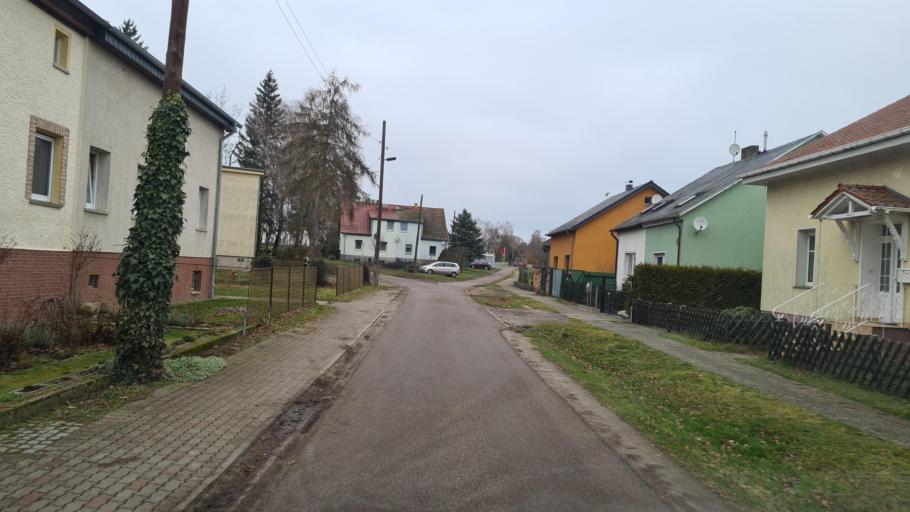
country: DE
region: Brandenburg
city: Zehdenick
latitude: 52.9346
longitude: 13.2607
